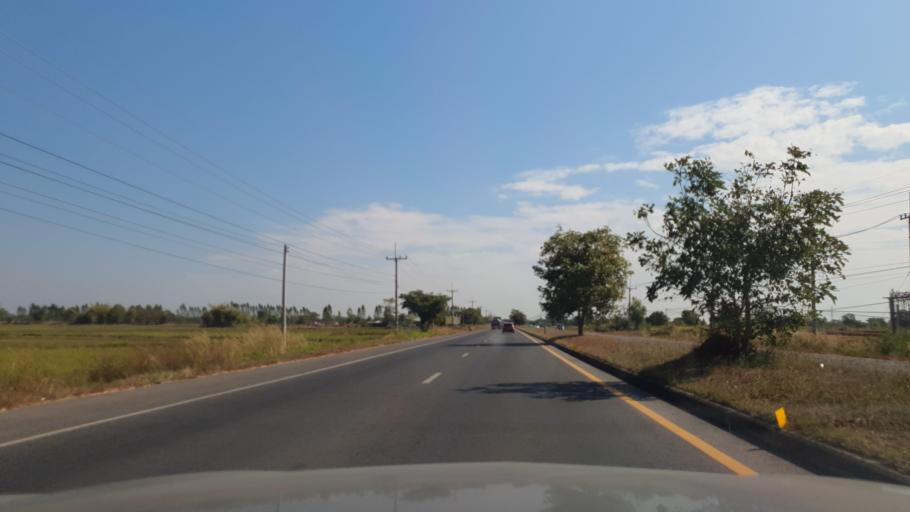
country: TH
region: Maha Sarakham
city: Chiang Yuen
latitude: 16.3753
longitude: 103.1634
